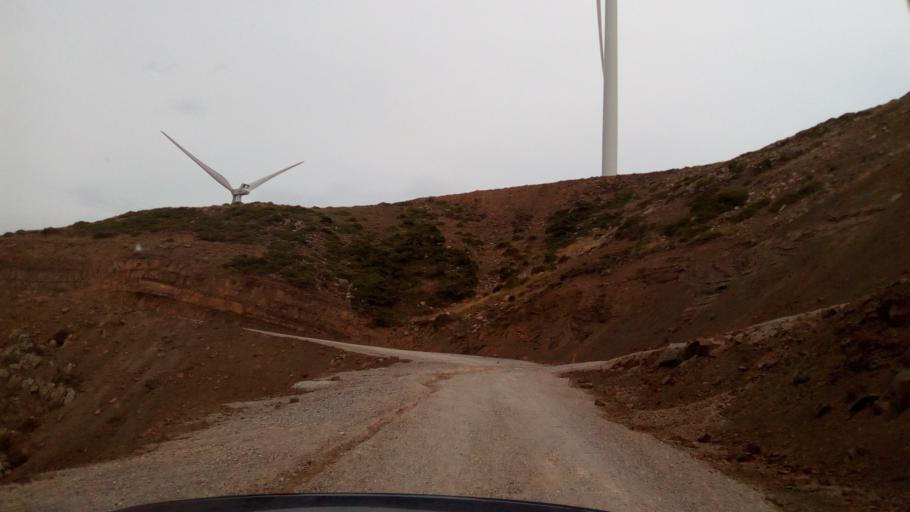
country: GR
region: Central Greece
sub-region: Nomos Fokidos
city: Lidoriki
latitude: 38.4563
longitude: 22.0757
